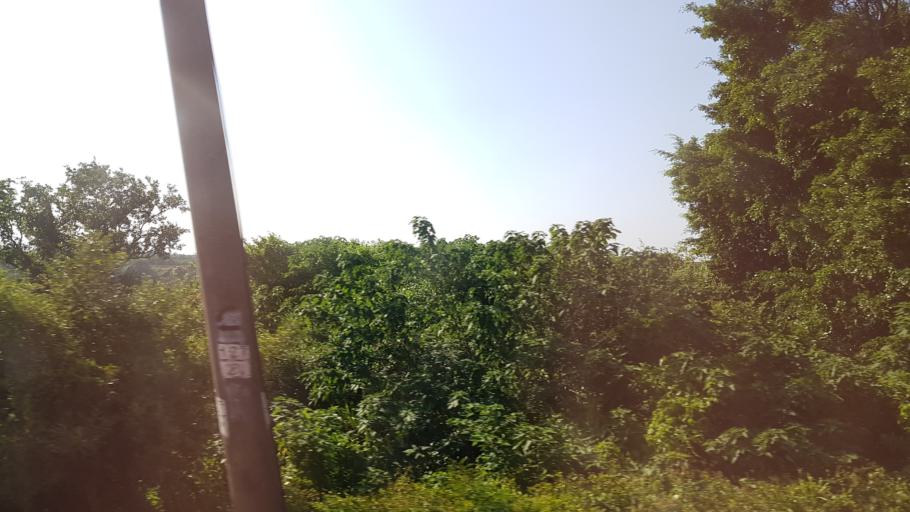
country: TW
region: Taiwan
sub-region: Miaoli
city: Miaoli
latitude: 24.6708
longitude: 120.8793
